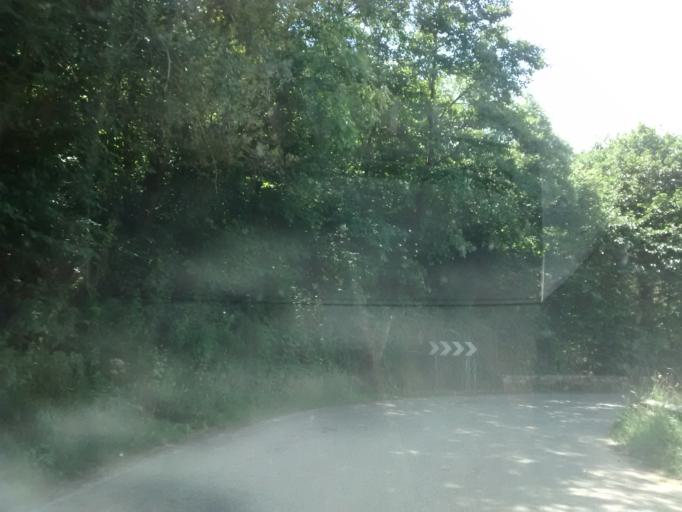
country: ES
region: Cantabria
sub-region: Provincia de Cantabria
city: Ruente
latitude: 43.1999
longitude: -4.3007
